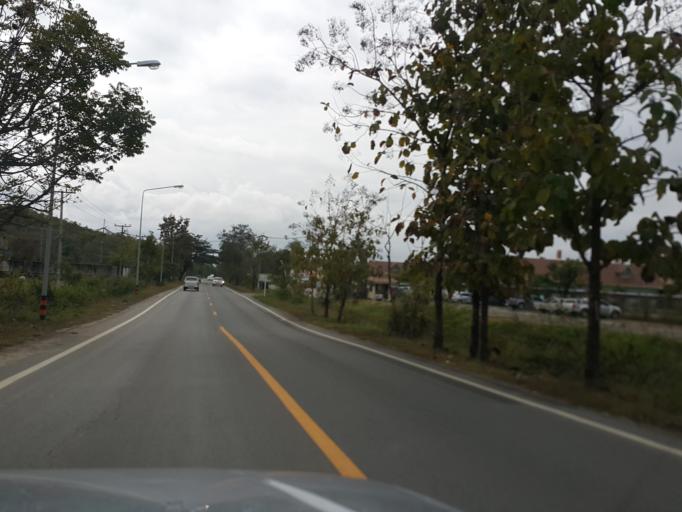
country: TH
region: Lamphun
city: Ban Thi
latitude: 18.6101
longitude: 99.0904
